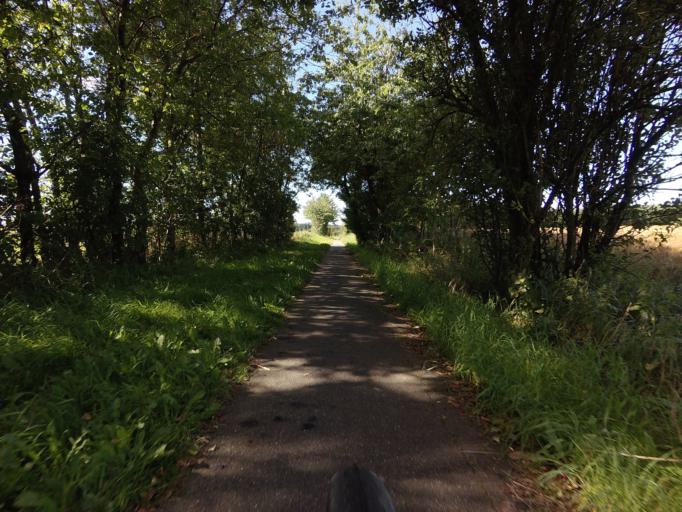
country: DK
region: Central Jutland
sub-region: Horsens Kommune
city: Braedstrup
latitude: 55.9772
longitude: 9.6389
